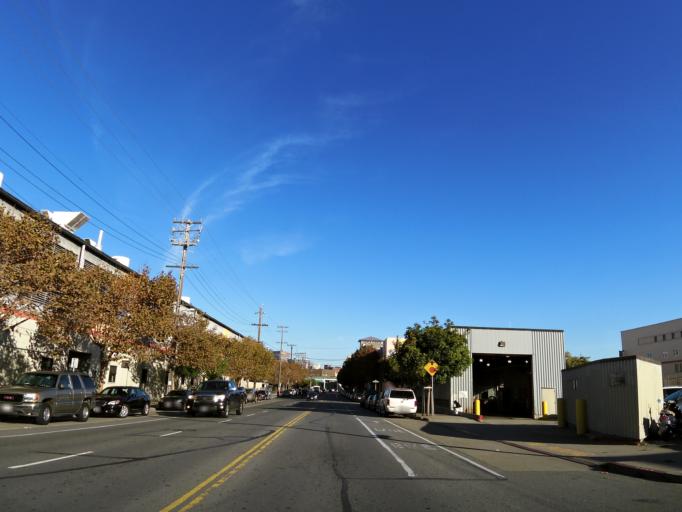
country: US
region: California
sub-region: San Francisco County
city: San Francisco
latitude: 37.7660
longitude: -122.4132
